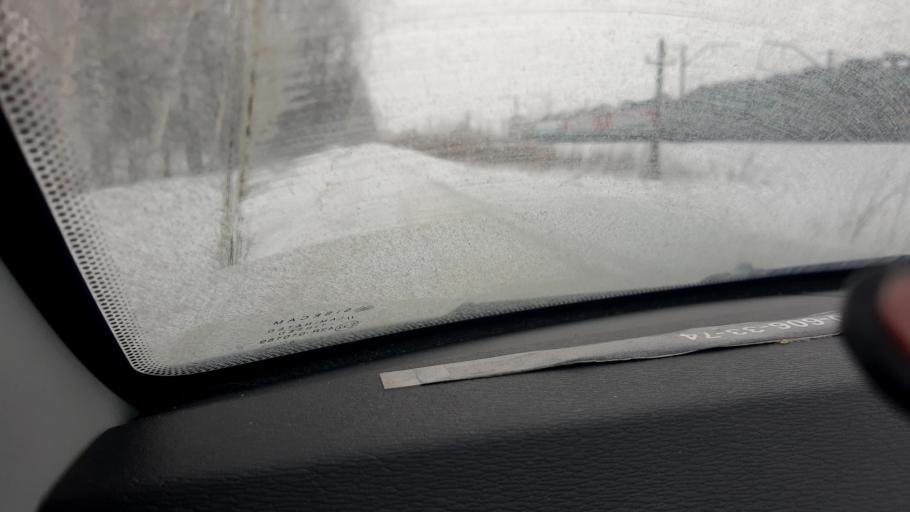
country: RU
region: Nizjnij Novgorod
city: Sitniki
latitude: 56.5262
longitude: 44.0535
